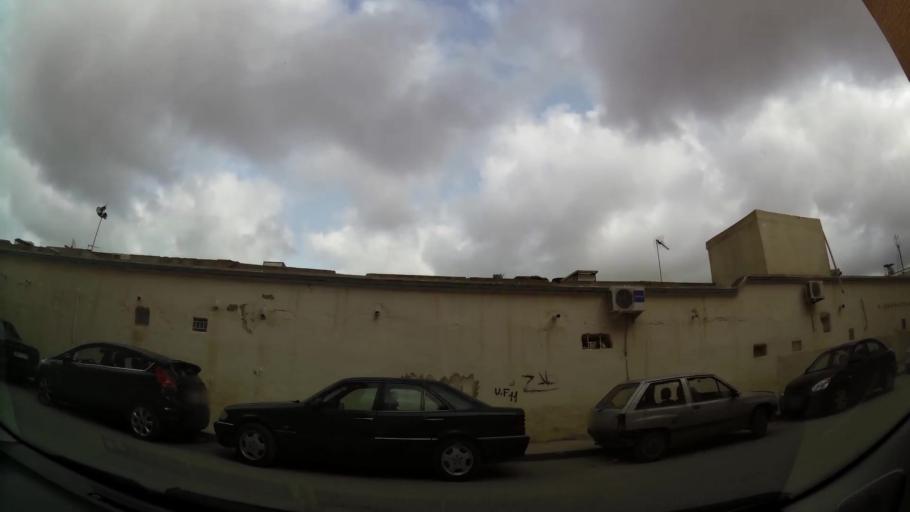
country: MA
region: Oriental
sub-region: Nador
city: Nador
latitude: 35.1711
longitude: -2.9364
